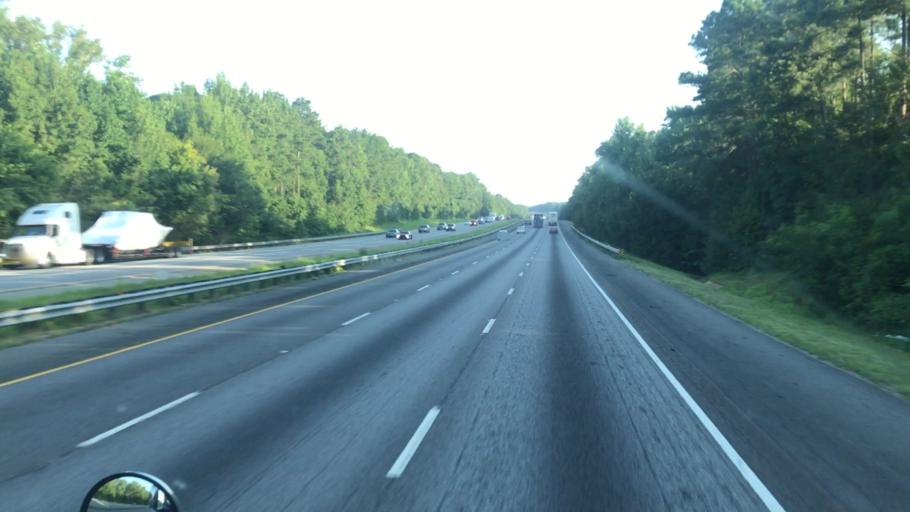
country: US
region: Georgia
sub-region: Henry County
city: Locust Grove
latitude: 33.2892
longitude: -84.1096
